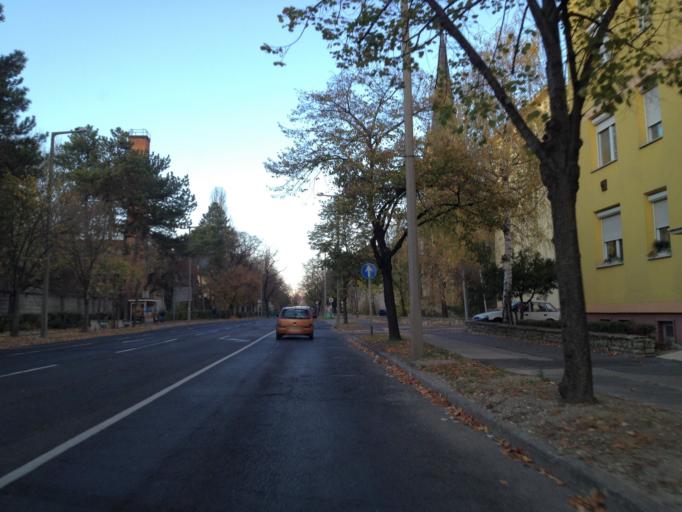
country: HU
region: Gyor-Moson-Sopron
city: Gyor
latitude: 47.6753
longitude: 17.6404
